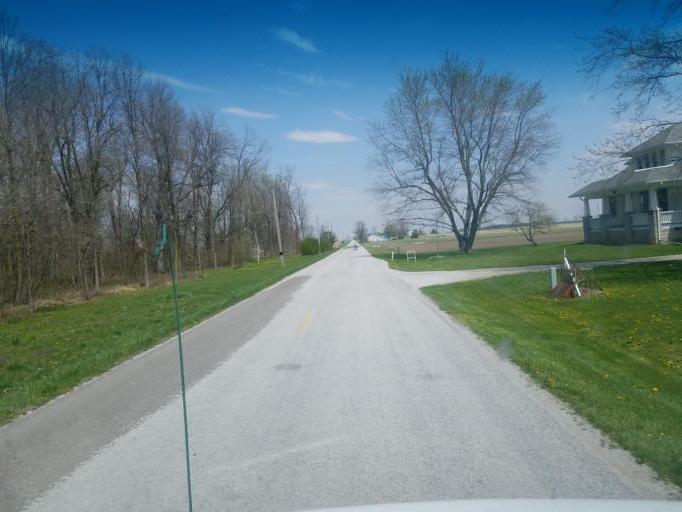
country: US
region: Ohio
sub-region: Hardin County
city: Forest
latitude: 40.7437
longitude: -83.5377
